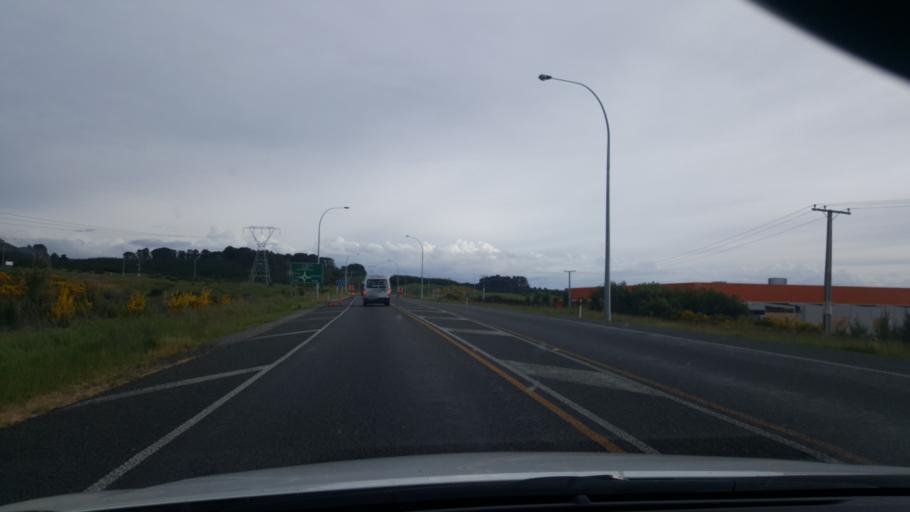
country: NZ
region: Waikato
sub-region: Taupo District
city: Taupo
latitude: -38.7014
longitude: 176.1118
